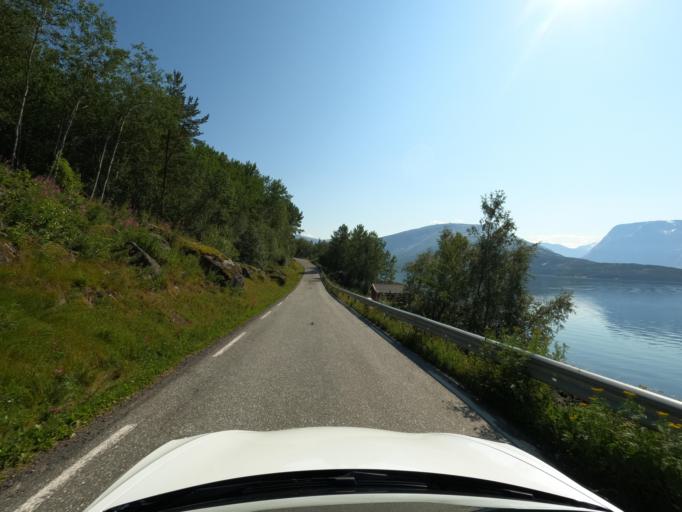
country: NO
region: Nordland
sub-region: Narvik
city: Narvik
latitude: 68.2774
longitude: 17.3889
